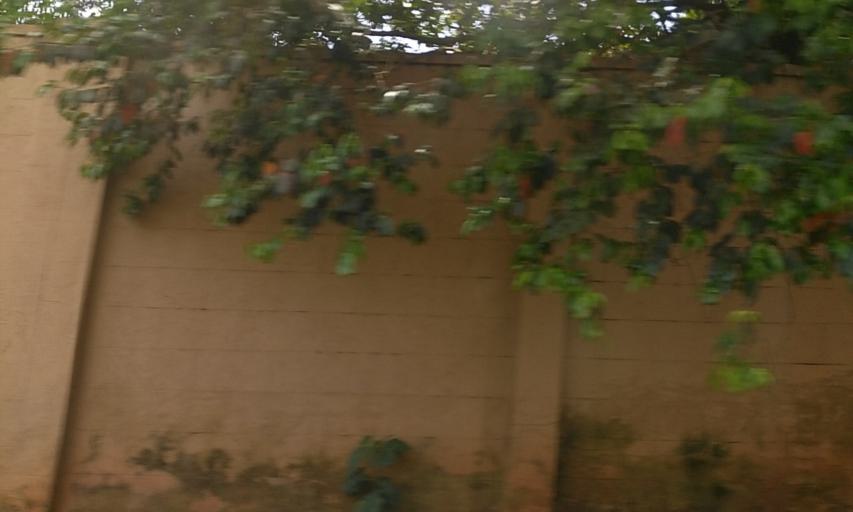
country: UG
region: Central Region
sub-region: Kampala District
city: Kampala
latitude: 0.3296
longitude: 32.6014
